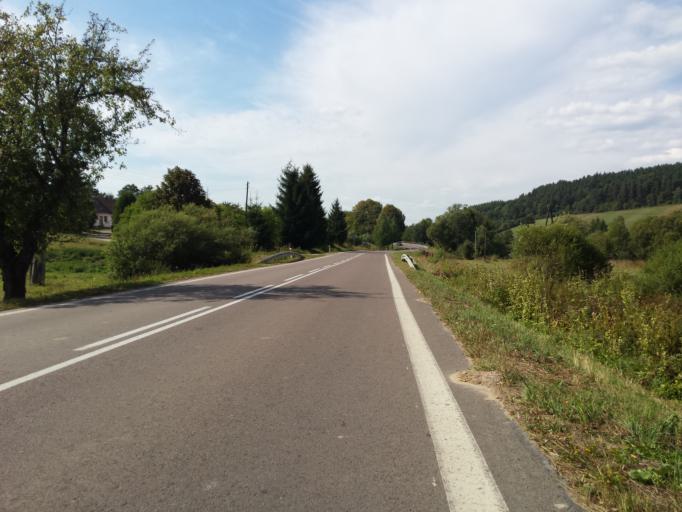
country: PL
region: Subcarpathian Voivodeship
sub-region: Powiat bieszczadzki
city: Ustrzyki Dolne
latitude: 49.5519
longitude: 22.5742
